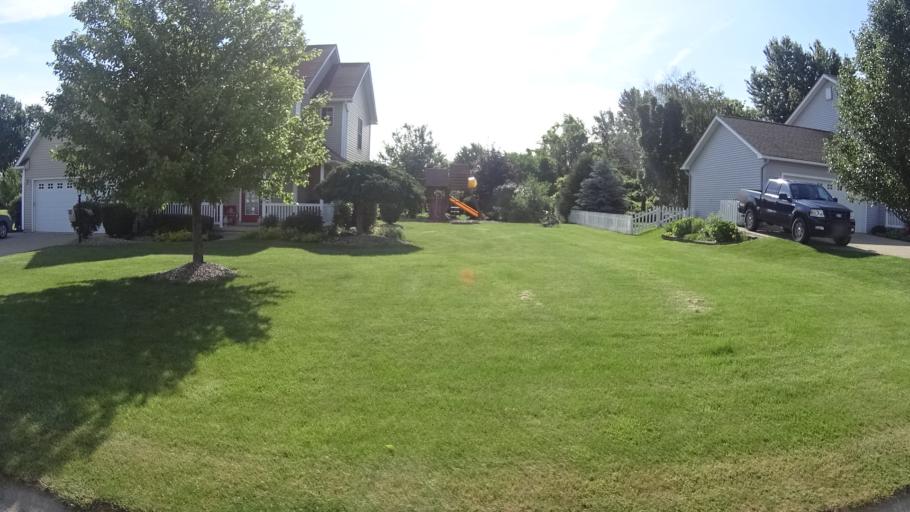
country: US
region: Ohio
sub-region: Erie County
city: Huron
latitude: 41.3812
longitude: -82.5230
